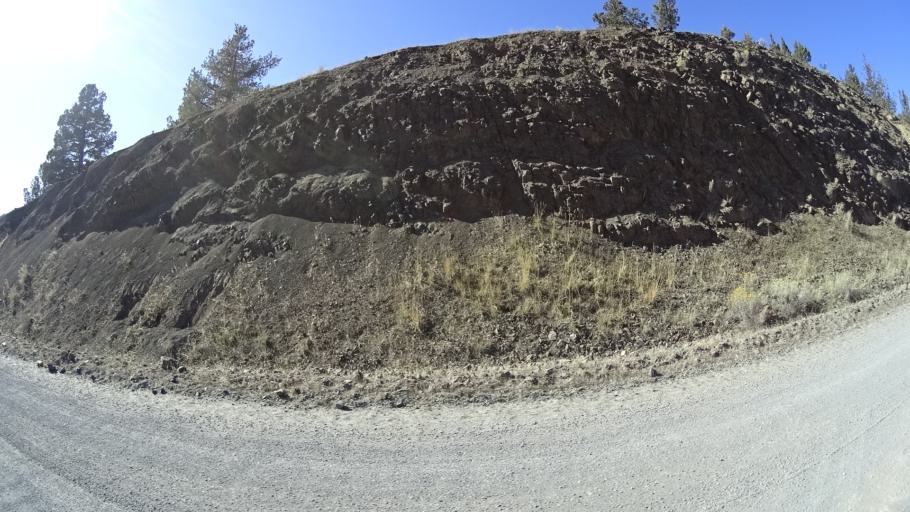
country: US
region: California
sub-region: Siskiyou County
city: Montague
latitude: 41.8057
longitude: -122.3713
